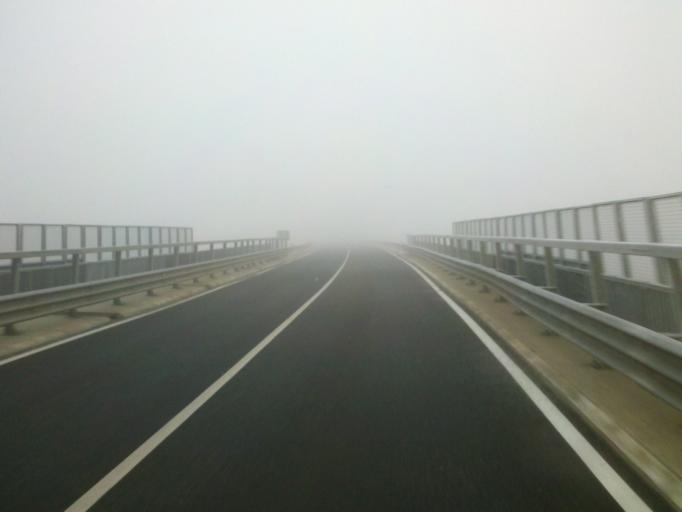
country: HR
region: Varazdinska
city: Jalkovec
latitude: 46.2851
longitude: 16.3110
